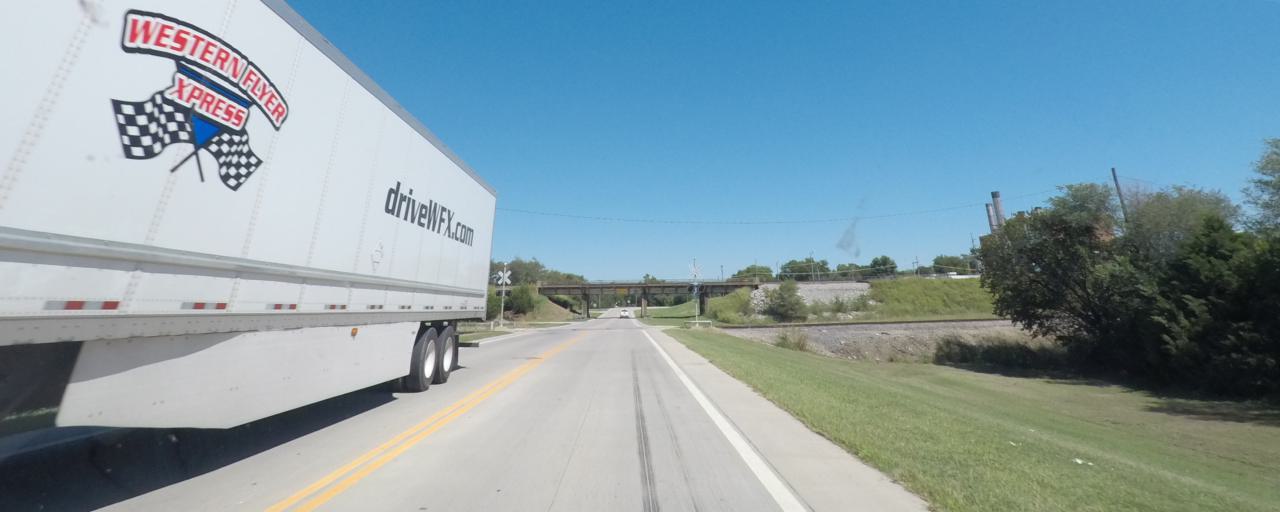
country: US
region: Kansas
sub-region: Sumner County
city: Wellington
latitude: 37.2594
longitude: -97.4070
